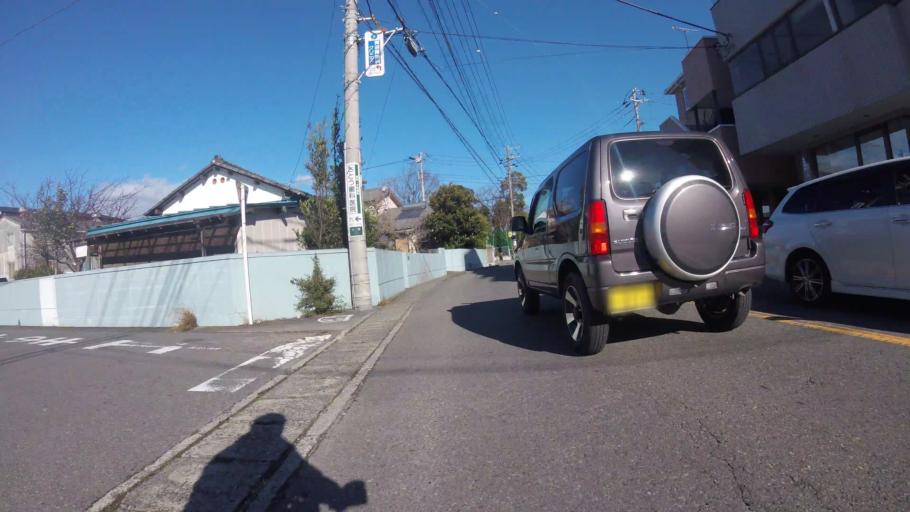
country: JP
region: Shizuoka
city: Numazu
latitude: 35.1116
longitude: 138.8800
